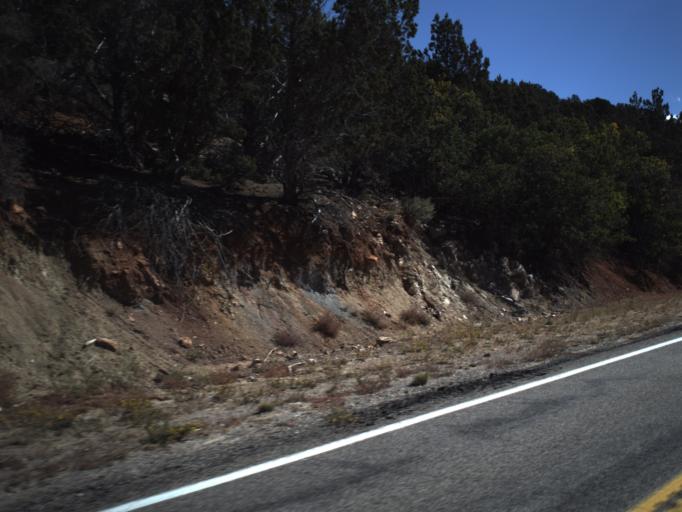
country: US
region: Utah
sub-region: Washington County
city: Enterprise
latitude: 37.5444
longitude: -113.6842
